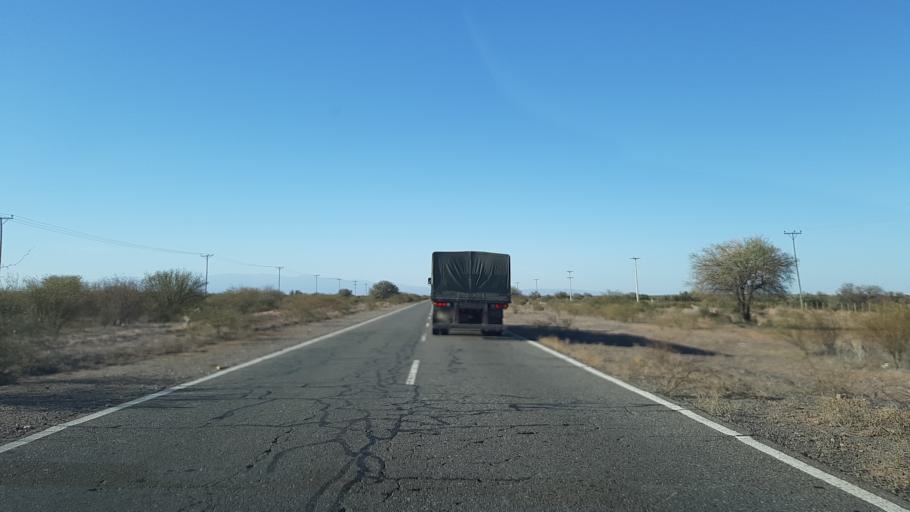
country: AR
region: San Juan
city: Caucete
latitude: -31.6480
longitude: -67.7623
